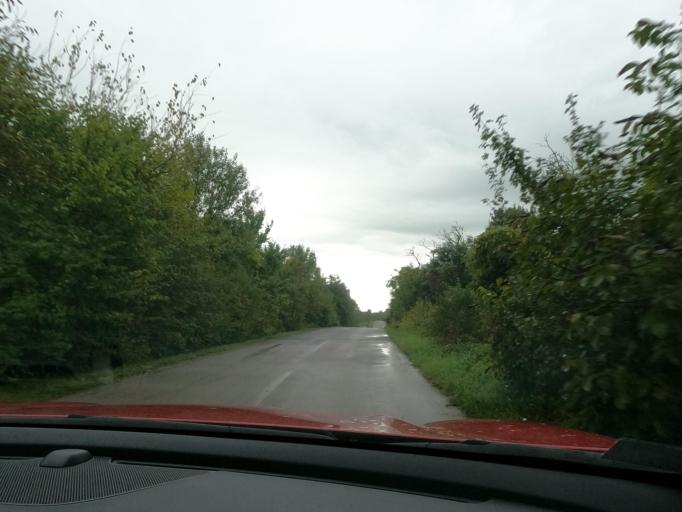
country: HR
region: Sisacko-Moslavacka
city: Glina
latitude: 45.3022
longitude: 16.1688
